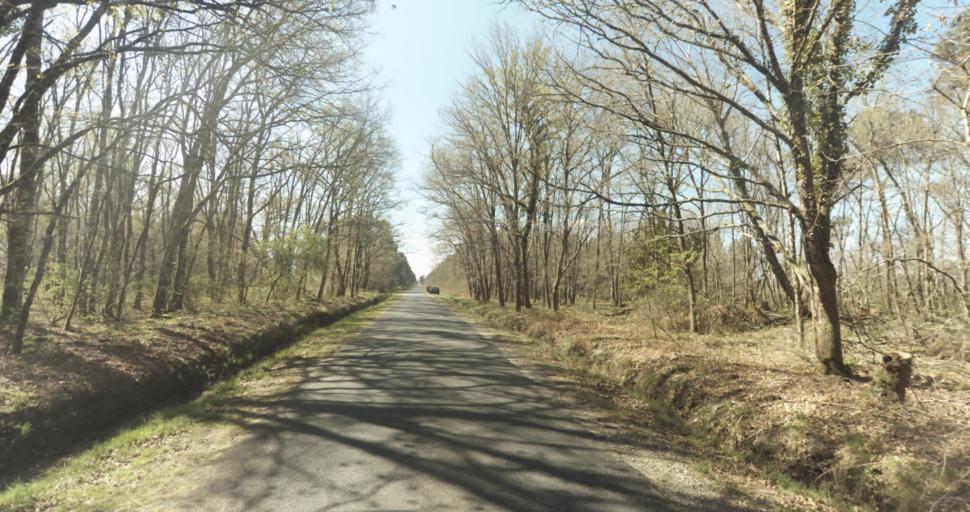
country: FR
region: Aquitaine
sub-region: Departement de la Gironde
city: Martignas-sur-Jalle
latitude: 44.7975
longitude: -0.7928
